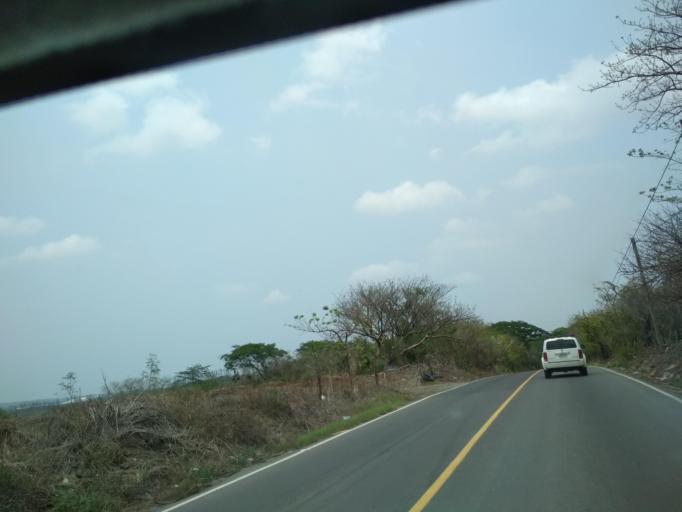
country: MX
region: Veracruz
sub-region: Veracruz
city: Delfino Victoria (Santa Fe)
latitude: 19.1696
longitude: -96.2839
